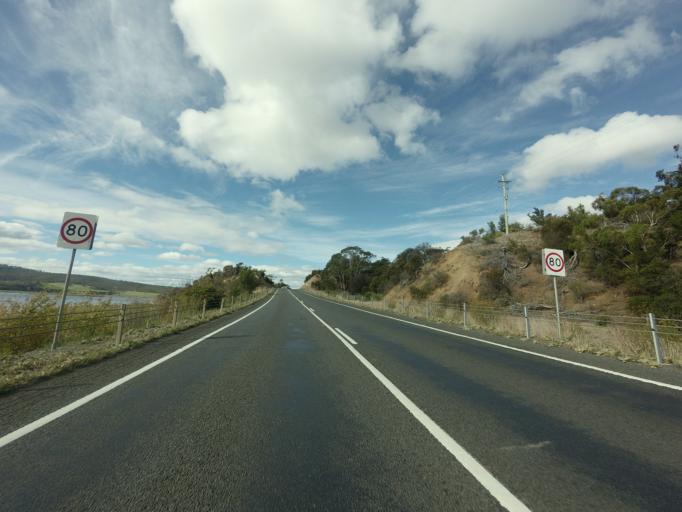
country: AU
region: Tasmania
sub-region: Glenorchy
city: Granton
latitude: -42.7447
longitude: 147.1849
